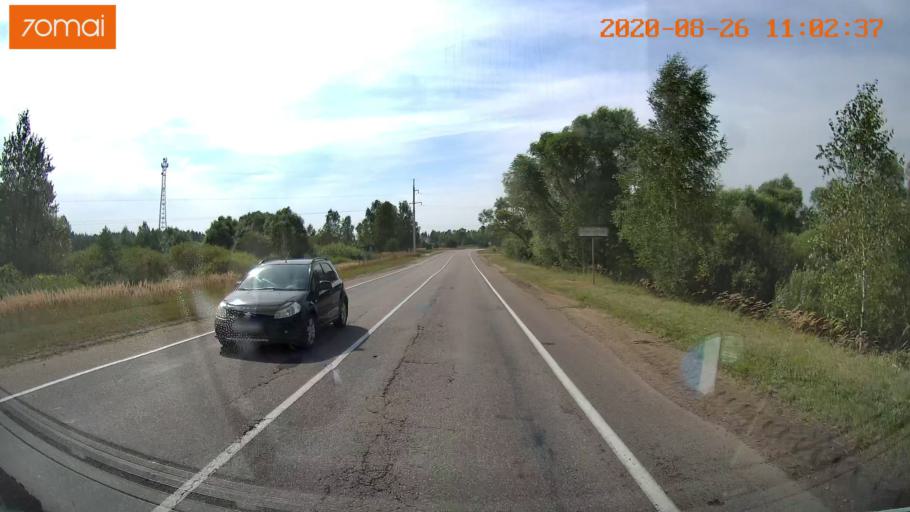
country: RU
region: Rjazan
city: Izhevskoye
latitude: 54.5483
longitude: 41.2233
